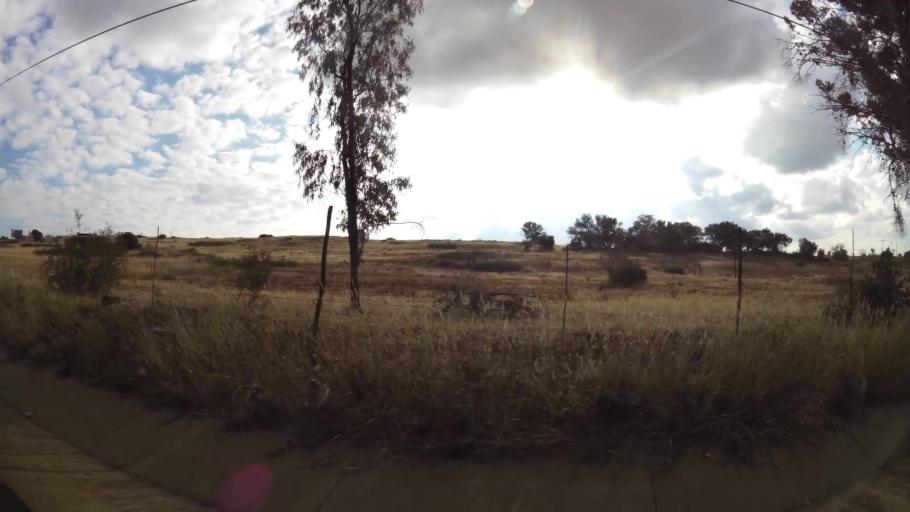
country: ZA
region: Orange Free State
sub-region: Mangaung Metropolitan Municipality
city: Bloemfontein
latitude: -29.0740
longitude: 26.1928
